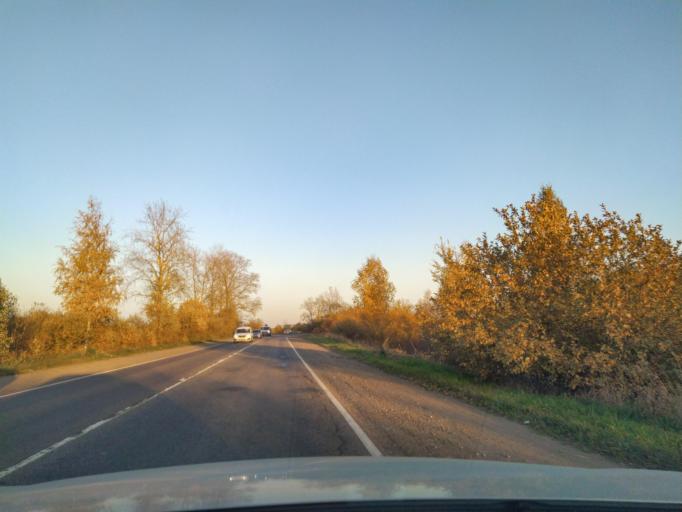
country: RU
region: Leningrad
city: Maloye Verevo
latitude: 59.6115
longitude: 30.2324
